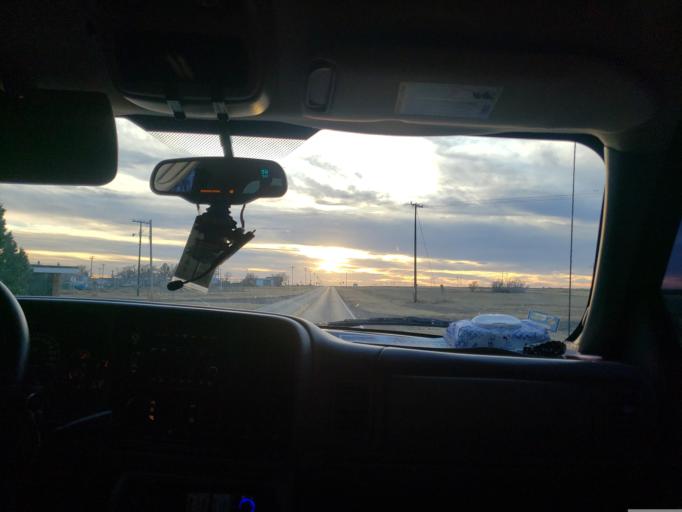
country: US
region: Oklahoma
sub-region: Cimarron County
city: Boise City
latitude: 36.8097
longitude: -102.2561
